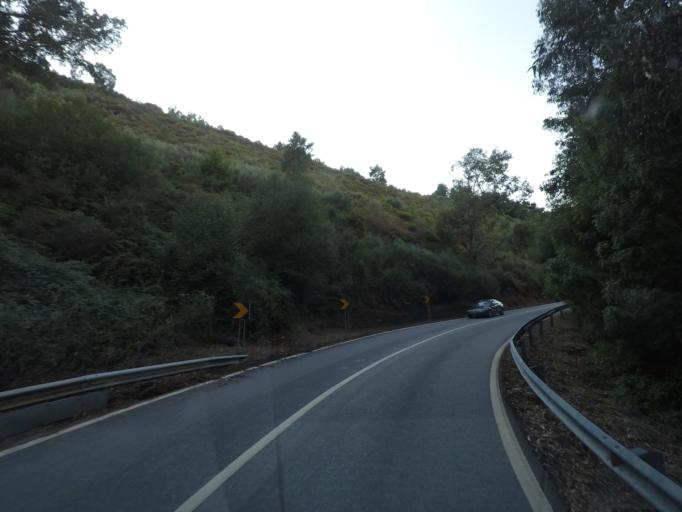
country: PT
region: Vila Real
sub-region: Mesao Frio
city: Mesao Frio
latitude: 41.1741
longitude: -7.9147
